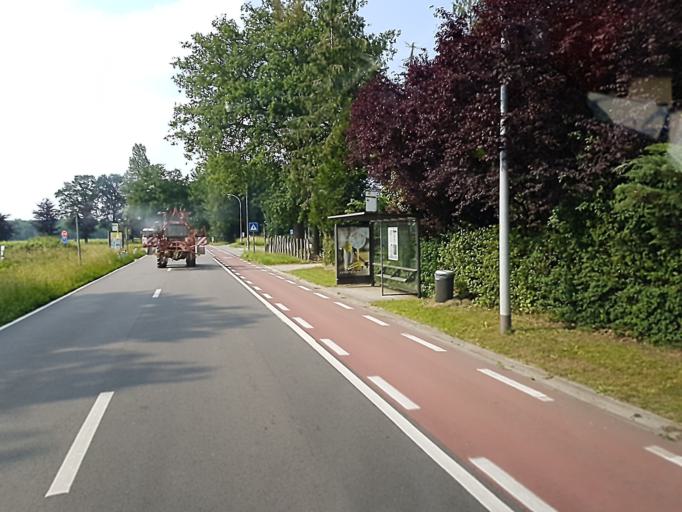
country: BE
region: Flanders
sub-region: Provincie Antwerpen
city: Turnhout
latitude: 51.3485
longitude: 4.9416
